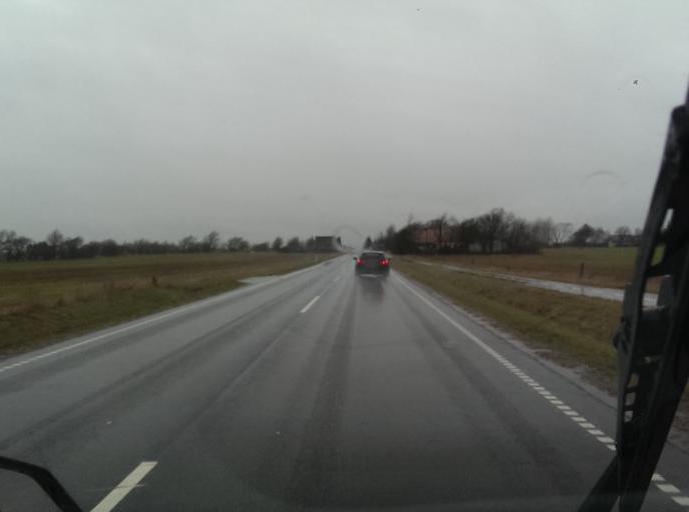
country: DK
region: South Denmark
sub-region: Varde Kommune
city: Olgod
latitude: 55.7443
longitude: 8.6189
